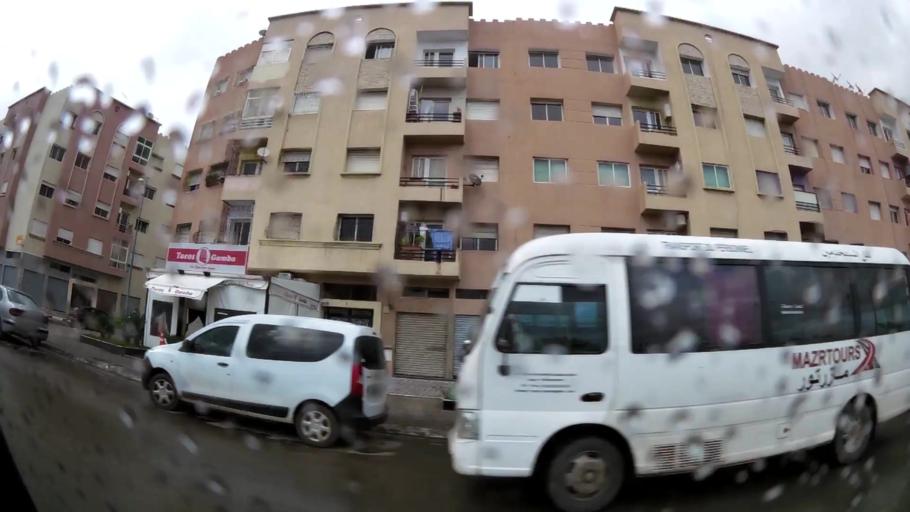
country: MA
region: Grand Casablanca
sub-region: Mohammedia
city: Mohammedia
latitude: 33.6797
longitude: -7.4021
